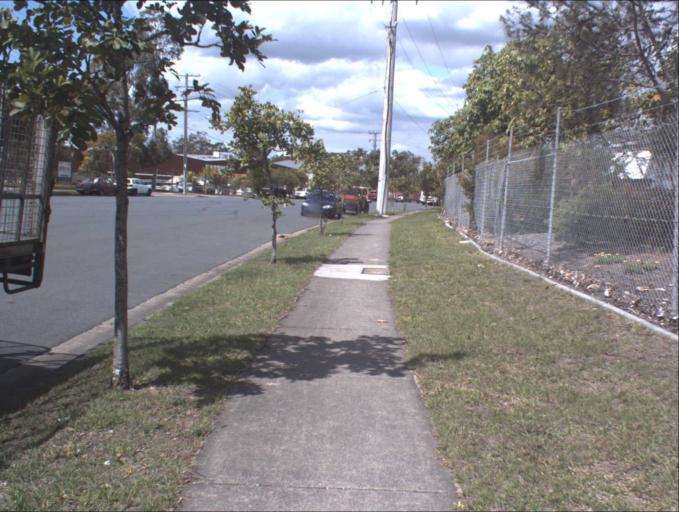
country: AU
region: Queensland
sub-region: Logan
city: Logan Reserve
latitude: -27.6779
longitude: 153.0781
